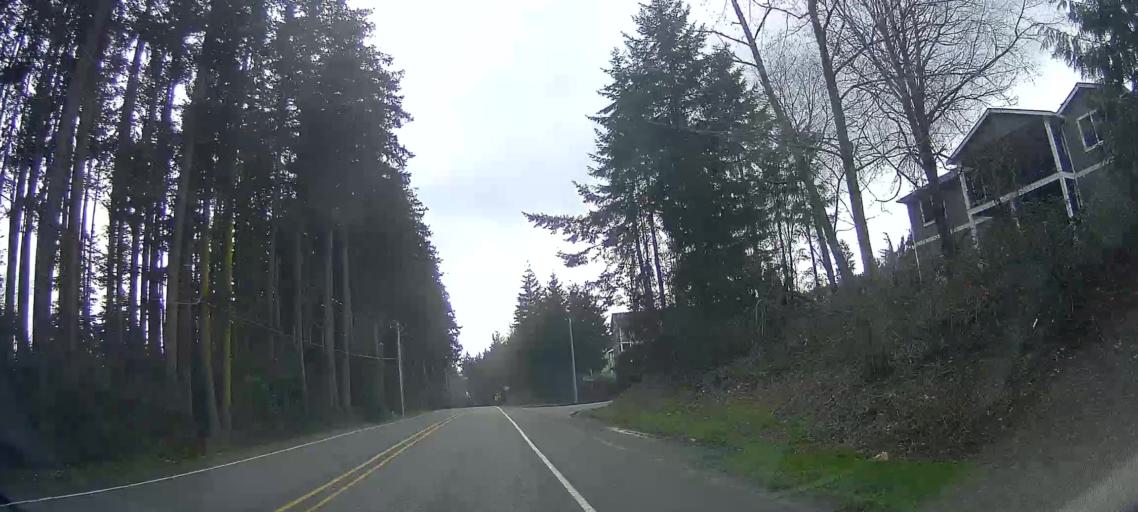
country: US
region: Washington
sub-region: Island County
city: Camano
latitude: 48.1707
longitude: -122.4808
